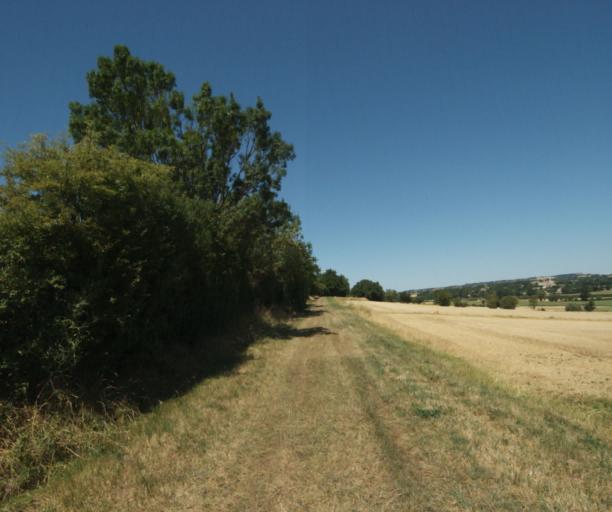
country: FR
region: Midi-Pyrenees
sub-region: Departement de la Haute-Garonne
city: Saint-Felix-Lauragais
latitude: 43.4655
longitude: 1.9230
